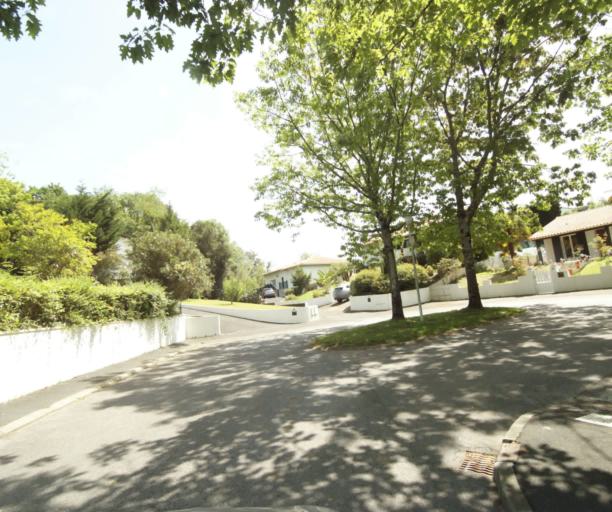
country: FR
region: Aquitaine
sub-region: Departement des Pyrenees-Atlantiques
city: Mouguerre
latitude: 43.4609
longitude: -1.4339
